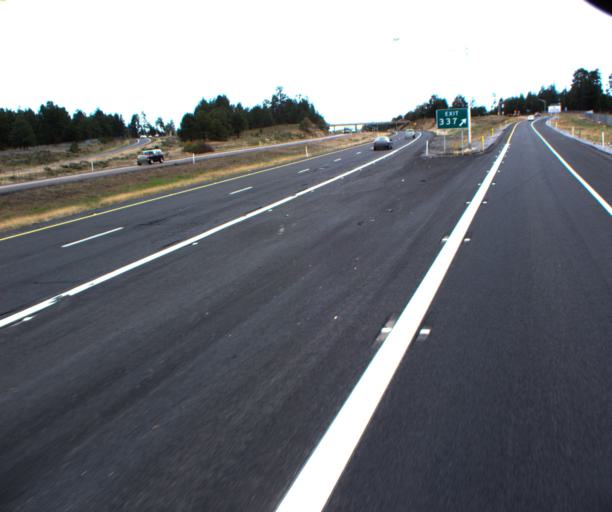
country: US
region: Arizona
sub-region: Coconino County
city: Kachina Village
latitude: 35.1436
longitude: -111.6843
